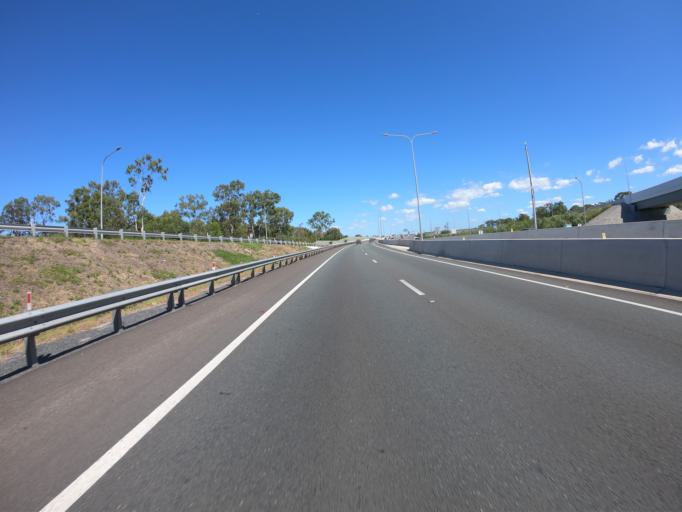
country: AU
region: Queensland
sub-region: Moreton Bay
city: Burpengary
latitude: -27.1520
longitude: 152.9820
